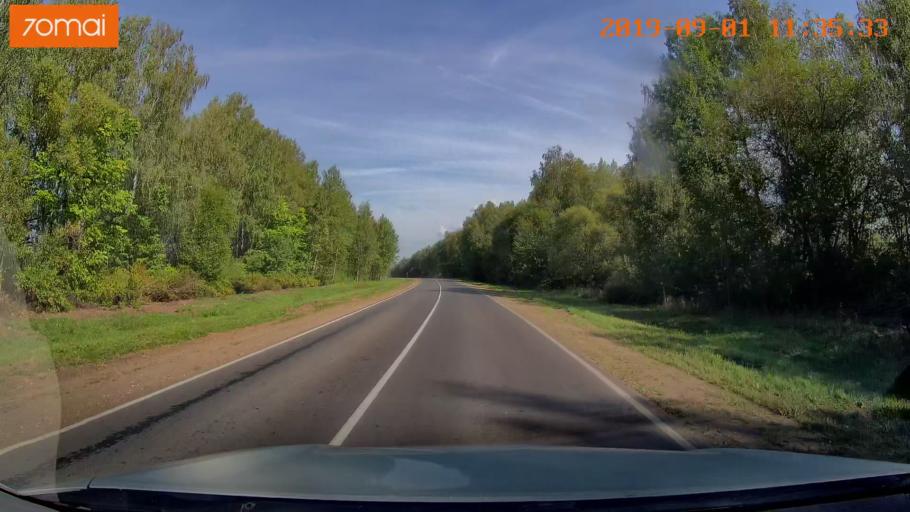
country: RU
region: Kaluga
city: Detchino
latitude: 54.8452
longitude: 36.3427
